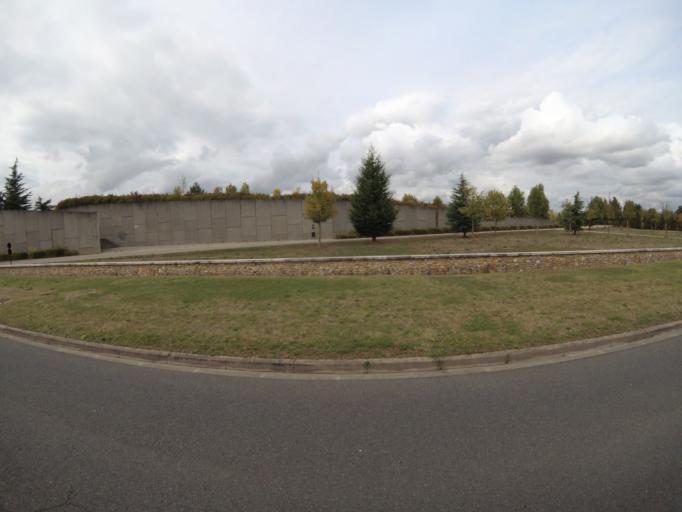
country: FR
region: Ile-de-France
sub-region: Departement de Seine-et-Marne
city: Chessy
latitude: 48.8712
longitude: 2.7637
